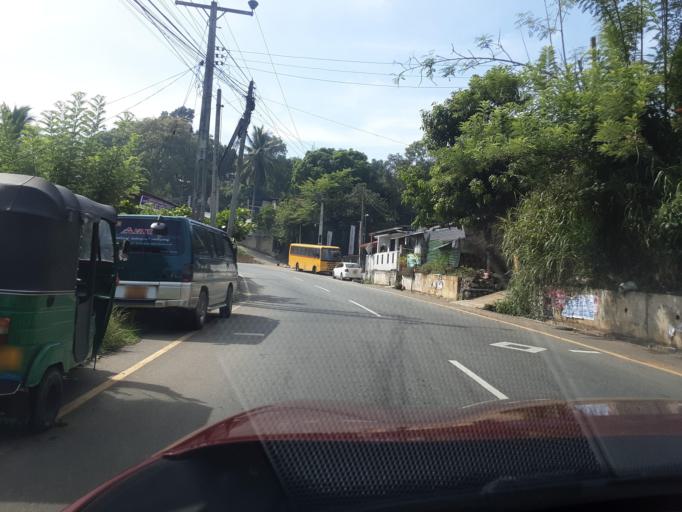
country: LK
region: Uva
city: Badulla
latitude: 6.9846
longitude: 81.0734
